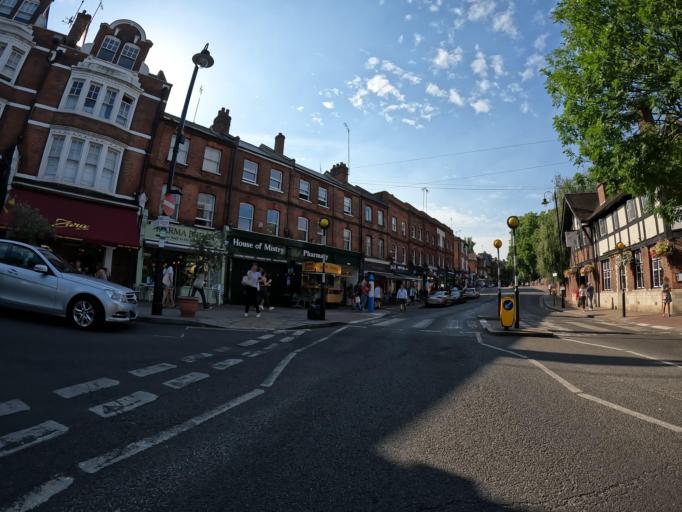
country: GB
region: England
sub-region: Greater London
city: Hendon
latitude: 51.6175
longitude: -0.2160
